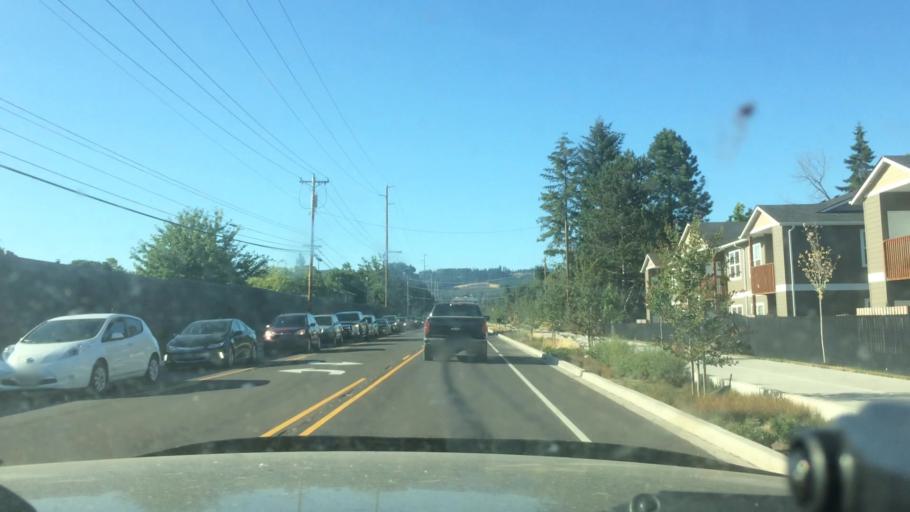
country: US
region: Oregon
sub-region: Yamhill County
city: Newberg
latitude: 45.2997
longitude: -122.9469
